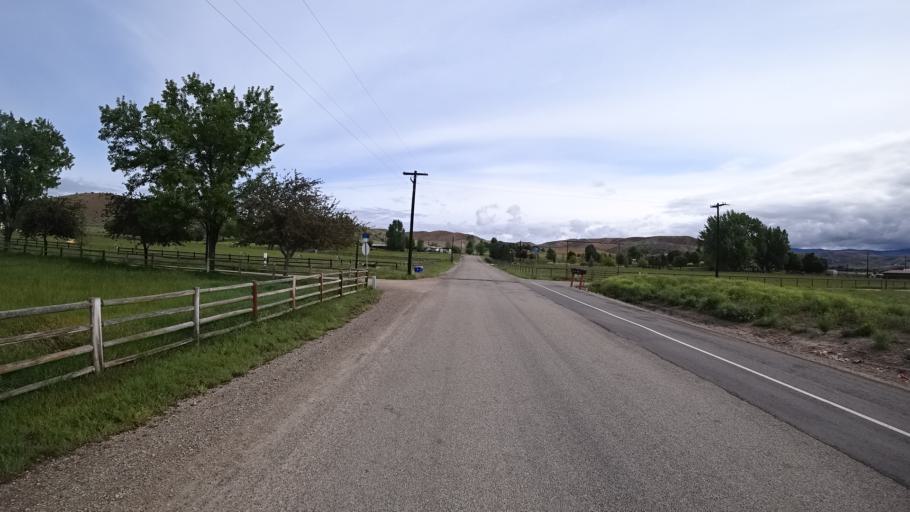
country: US
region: Idaho
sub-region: Ada County
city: Eagle
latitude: 43.7281
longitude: -116.3192
